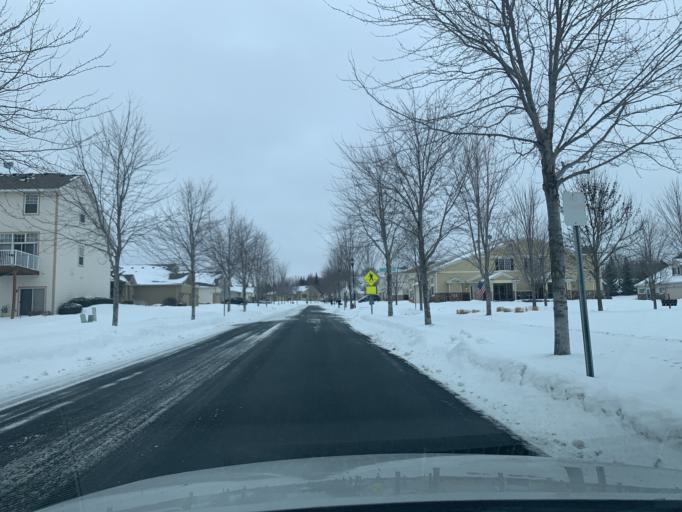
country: US
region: Minnesota
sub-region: Carver County
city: Victoria
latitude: 44.8391
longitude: -93.6546
